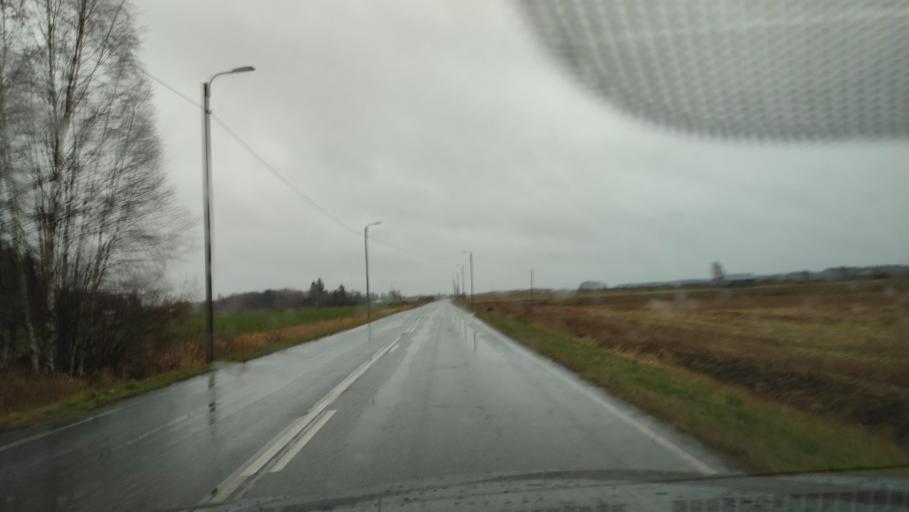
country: FI
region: Ostrobothnia
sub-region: Vaasa
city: Ristinummi
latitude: 63.0475
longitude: 21.7411
